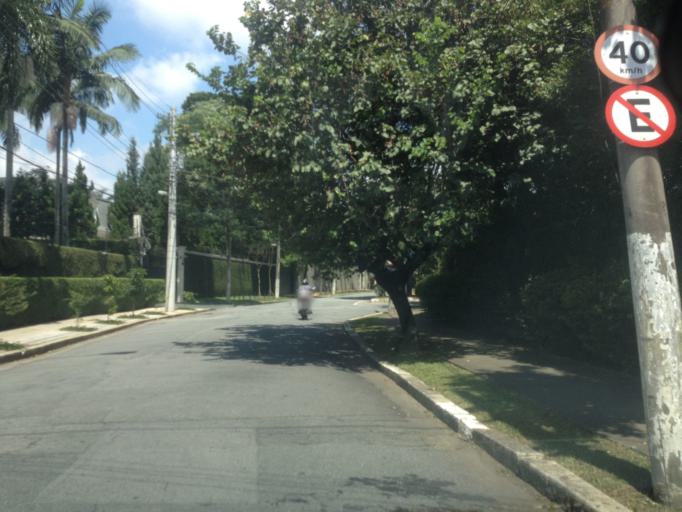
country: BR
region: Sao Paulo
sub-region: Sao Paulo
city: Sao Paulo
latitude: -23.5705
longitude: -46.6740
